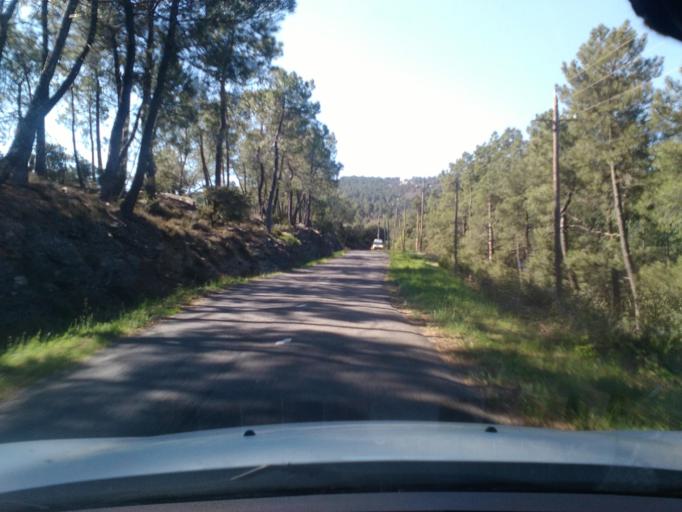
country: FR
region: Languedoc-Roussillon
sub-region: Departement du Gard
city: Valleraugue
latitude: 44.1684
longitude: 3.7517
